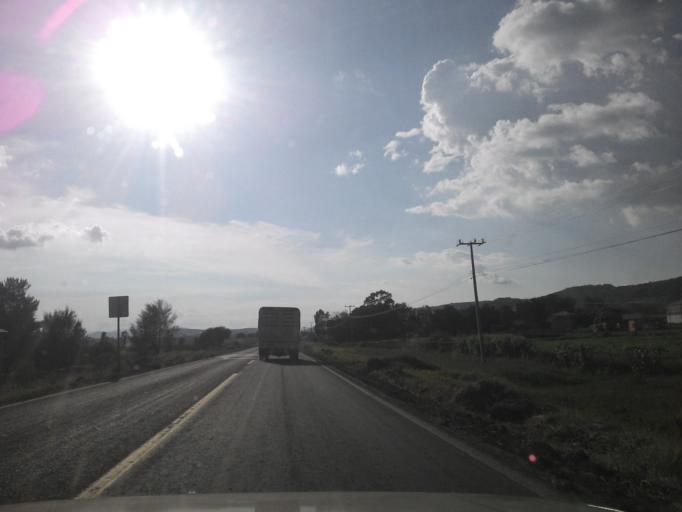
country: MX
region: Jalisco
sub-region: Atotonilco el Alto
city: San Francisco de Asis
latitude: 20.5418
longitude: -102.5811
